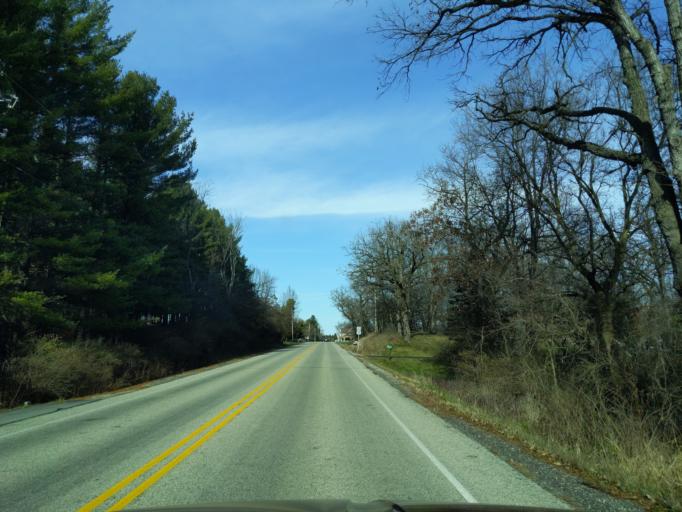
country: US
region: Wisconsin
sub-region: Jefferson County
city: Palmyra
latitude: 42.7971
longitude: -88.6025
